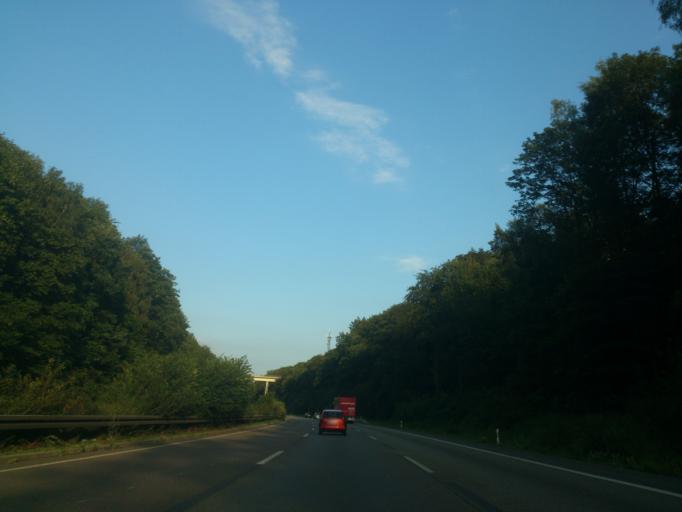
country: DE
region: North Rhine-Westphalia
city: Herdecke
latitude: 51.4463
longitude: 7.4301
